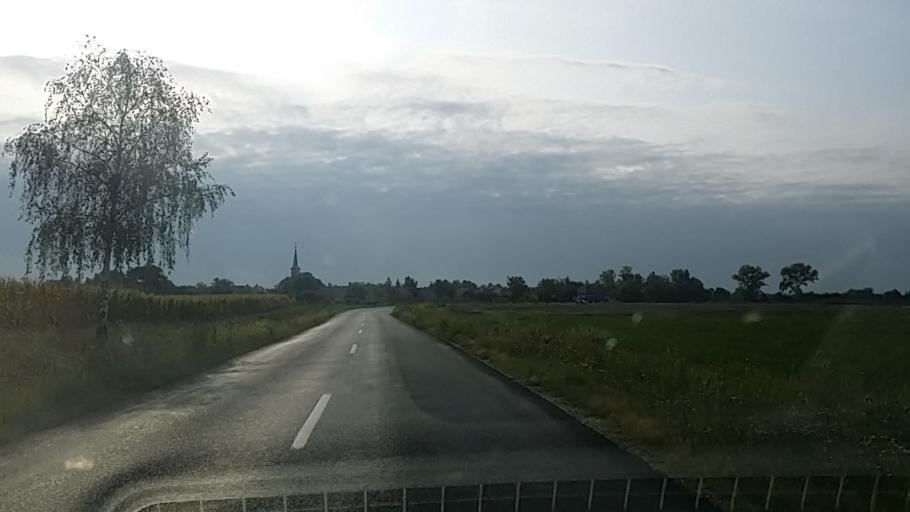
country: HU
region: Gyor-Moson-Sopron
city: Fertoszentmiklos
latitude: 47.6093
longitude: 16.8990
